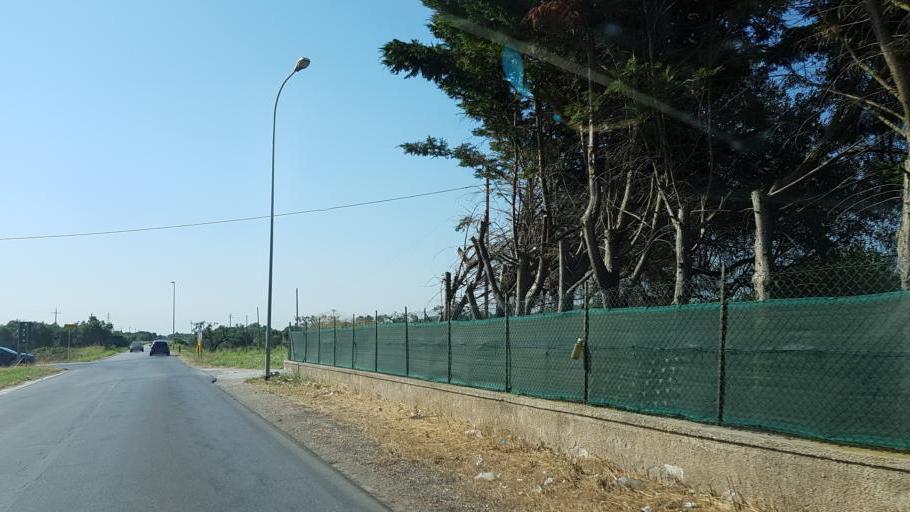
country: IT
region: Apulia
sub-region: Provincia di Brindisi
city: Mesagne
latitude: 40.5450
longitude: 17.8224
